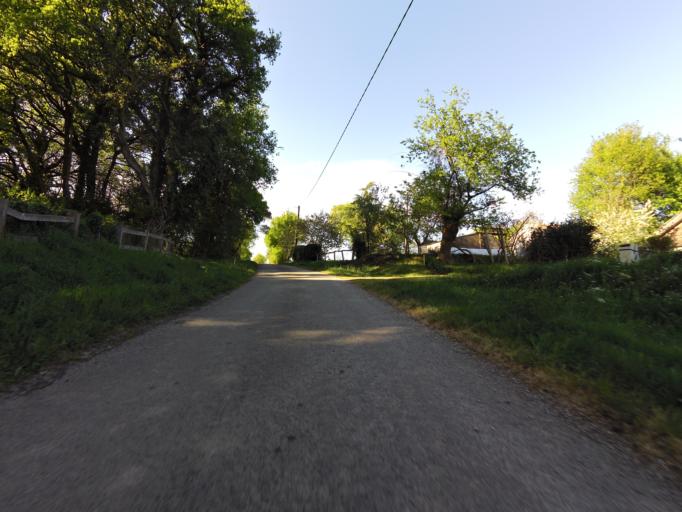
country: FR
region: Brittany
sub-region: Departement du Morbihan
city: Molac
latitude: 47.7361
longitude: -2.4759
